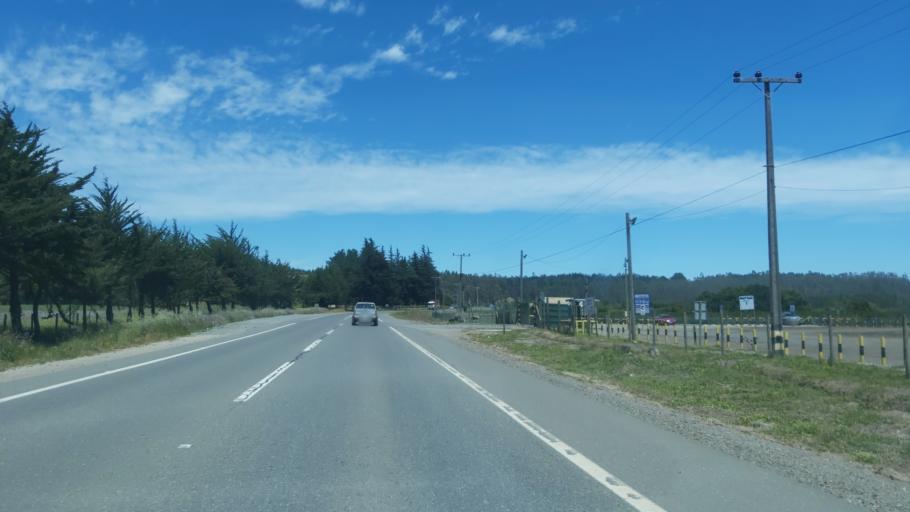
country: CL
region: Maule
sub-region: Provincia de Talca
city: Constitucion
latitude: -35.3104
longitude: -72.3813
